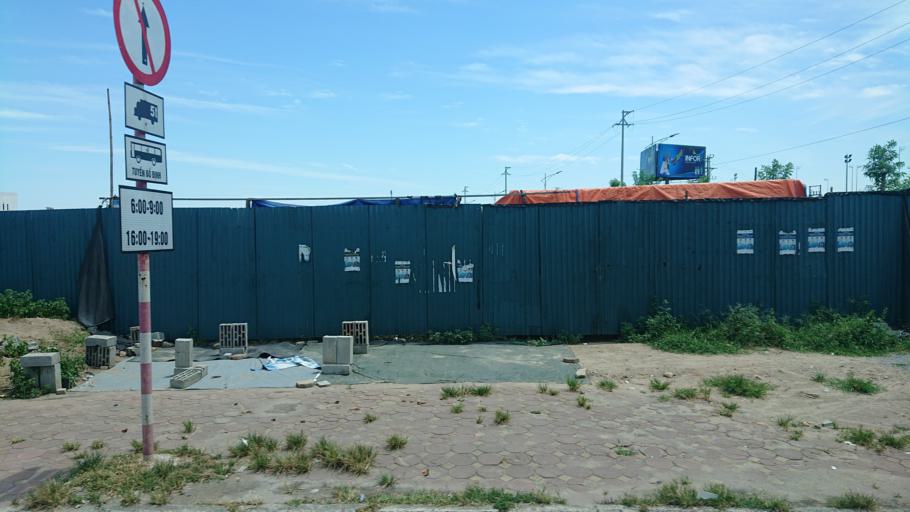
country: VN
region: Ha Nam
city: Thanh Pho Phu Ly
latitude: 20.5393
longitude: 105.9467
